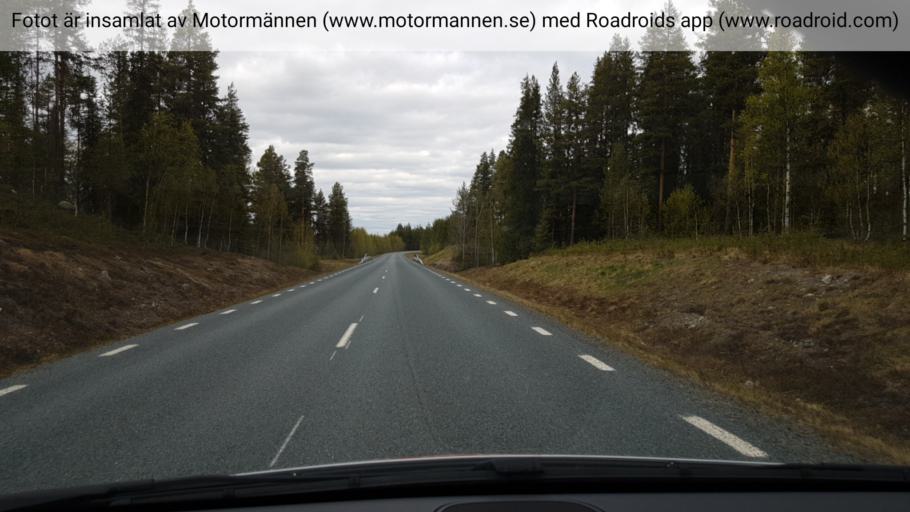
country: SE
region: Vaesterbotten
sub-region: Lycksele Kommun
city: Soderfors
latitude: 65.1723
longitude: 18.2508
